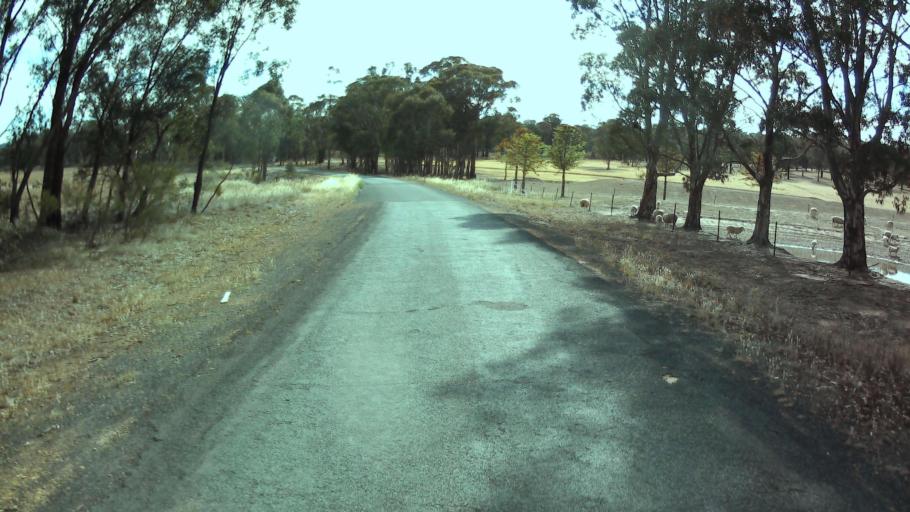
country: AU
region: New South Wales
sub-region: Weddin
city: Grenfell
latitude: -33.8490
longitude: 148.2320
